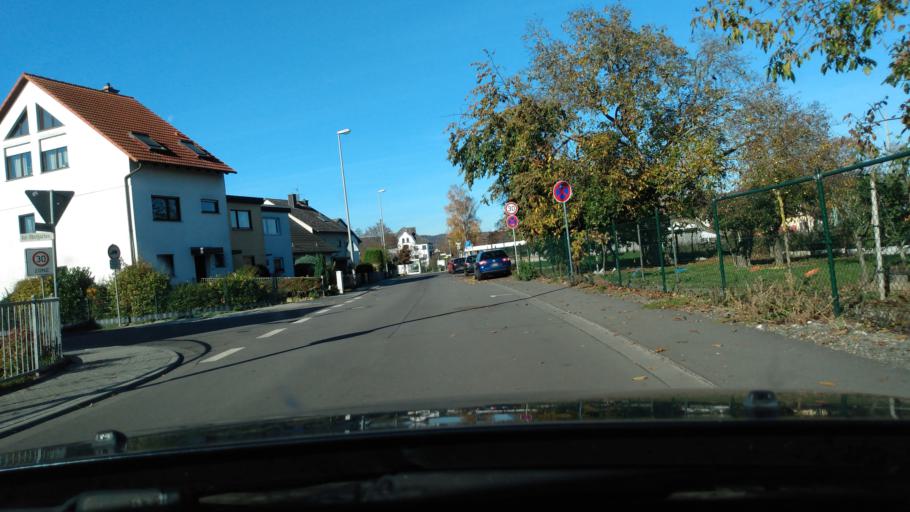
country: DE
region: Hesse
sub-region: Regierungsbezirk Darmstadt
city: Hattersheim
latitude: 50.0813
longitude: 8.4765
